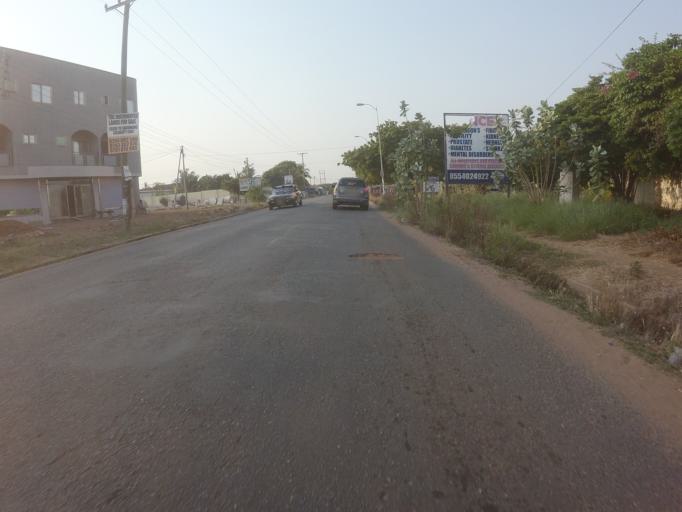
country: GH
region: Greater Accra
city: Nungua
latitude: 5.6198
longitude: -0.0549
